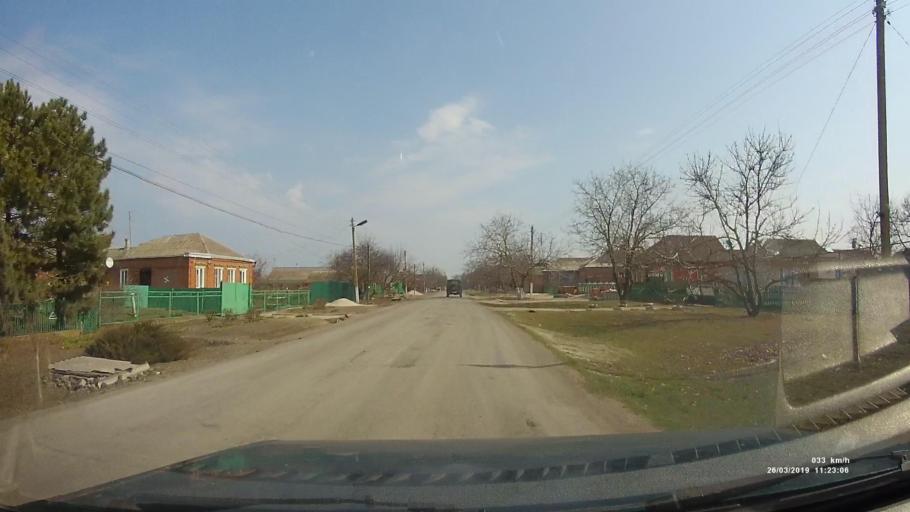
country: RU
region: Rostov
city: Novobessergenovka
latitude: 47.1394
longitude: 38.5580
